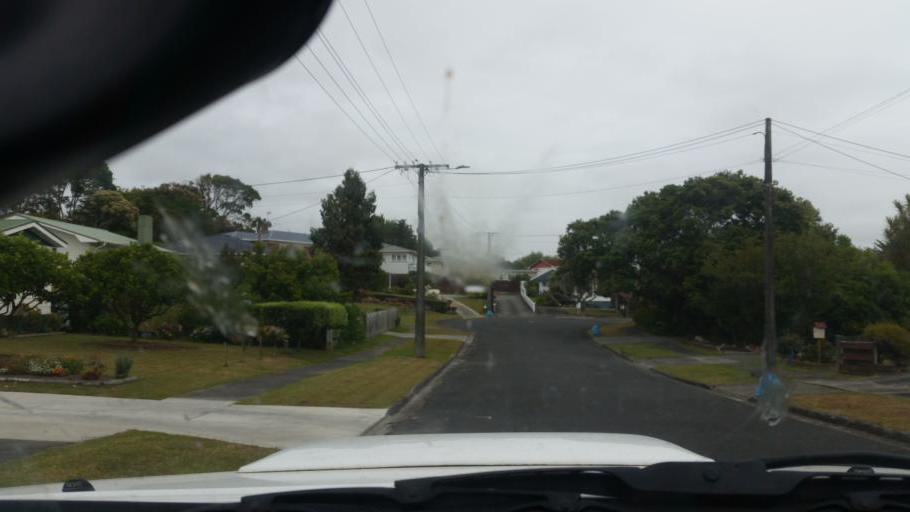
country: NZ
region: Northland
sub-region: Kaipara District
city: Dargaville
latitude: -35.9335
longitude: 173.8633
